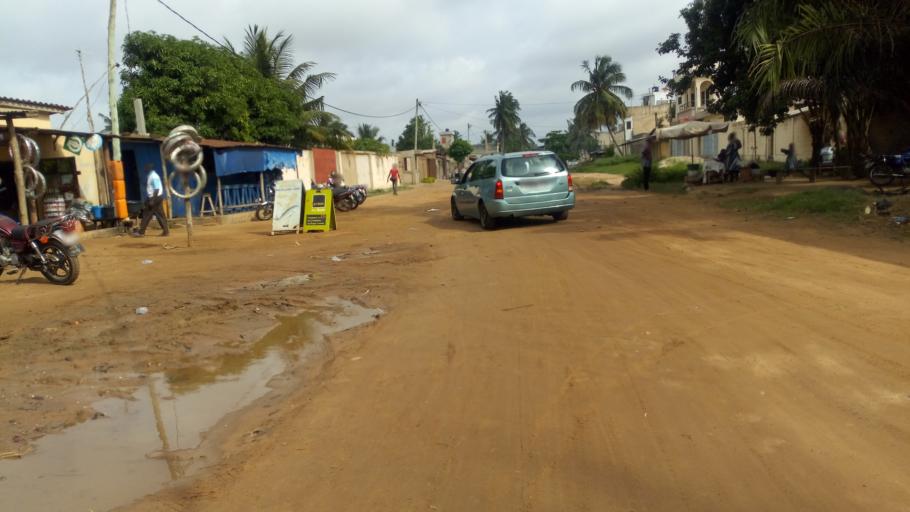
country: TG
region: Maritime
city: Lome
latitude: 6.1766
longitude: 1.1686
